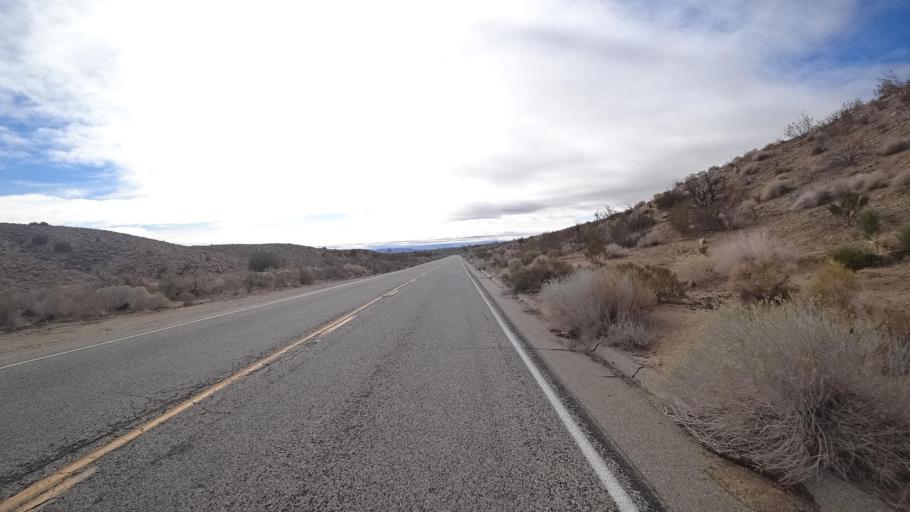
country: US
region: California
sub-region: Kern County
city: Tehachapi
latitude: 35.0085
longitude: -118.3403
